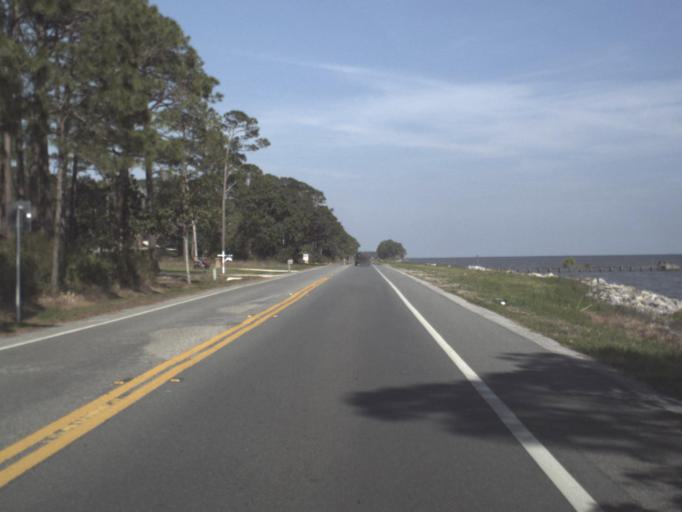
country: US
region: Florida
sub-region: Franklin County
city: Eastpoint
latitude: 29.7458
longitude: -84.8610
